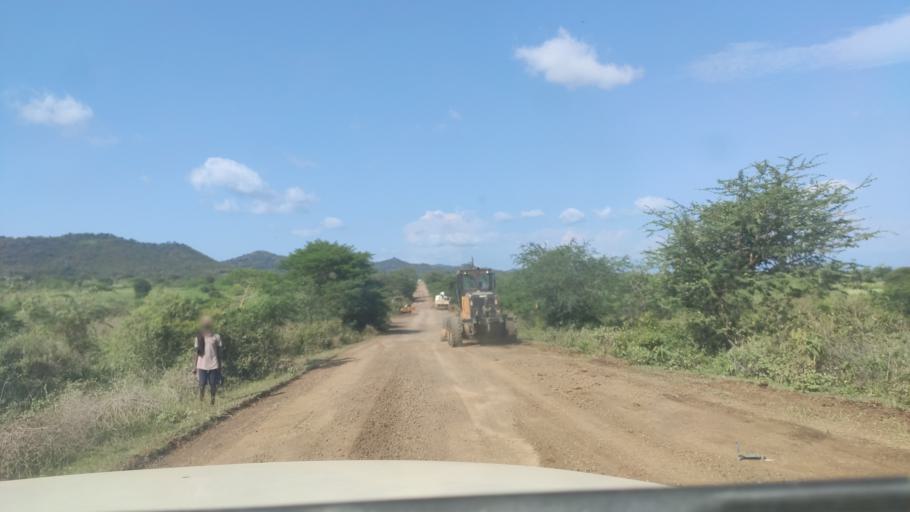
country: ET
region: Southern Nations, Nationalities, and People's Region
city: Felege Neway
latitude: 6.3876
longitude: 37.0966
